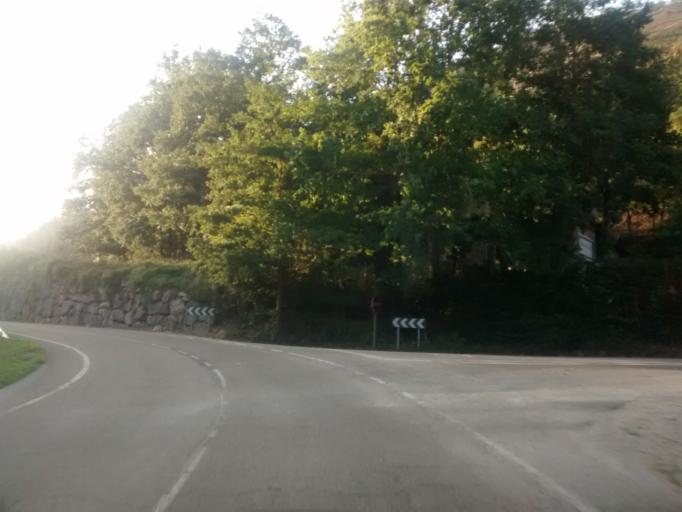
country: ES
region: Cantabria
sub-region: Provincia de Cantabria
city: Ruente
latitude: 43.1559
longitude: -4.2345
